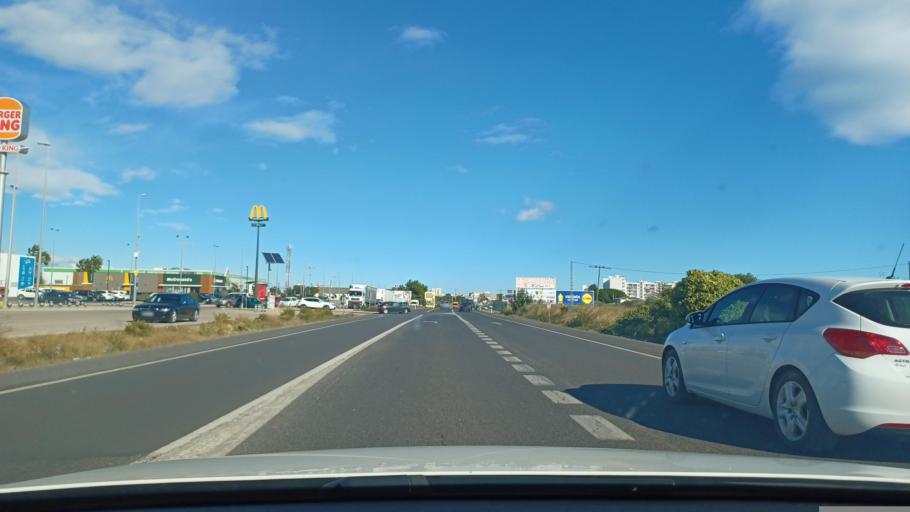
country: ES
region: Valencia
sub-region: Provincia de Castello
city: Vinaros
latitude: 40.4539
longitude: 0.4529
